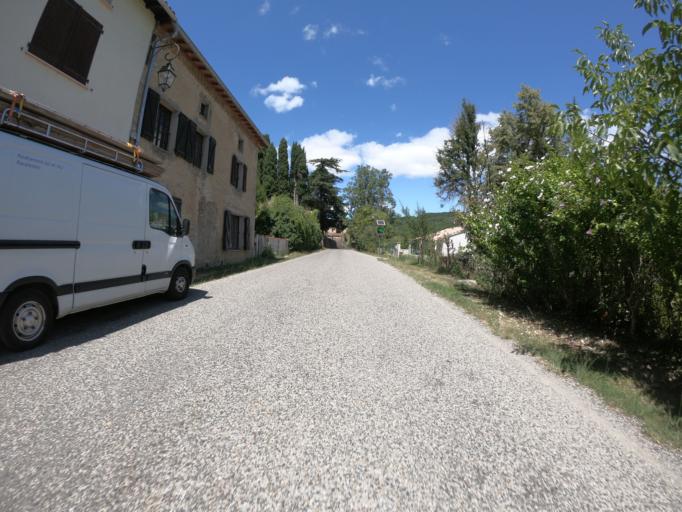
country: FR
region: Midi-Pyrenees
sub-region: Departement de l'Ariege
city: Verniolle
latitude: 43.0493
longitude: 1.7596
